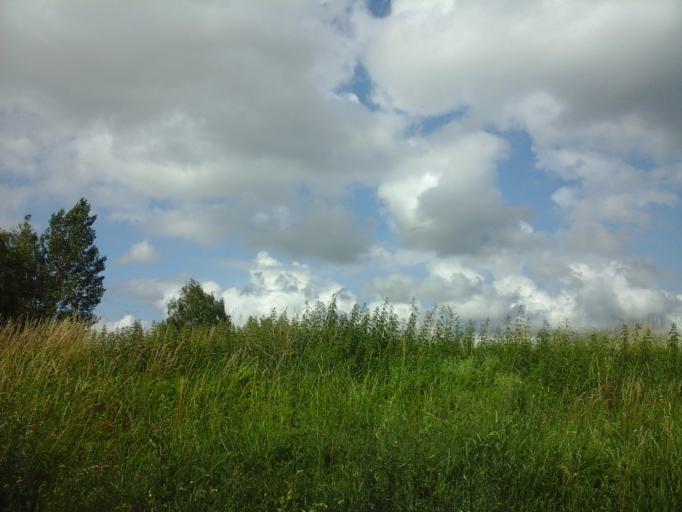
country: PL
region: West Pomeranian Voivodeship
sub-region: Powiat choszczenski
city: Choszczno
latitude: 53.1615
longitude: 15.4390
